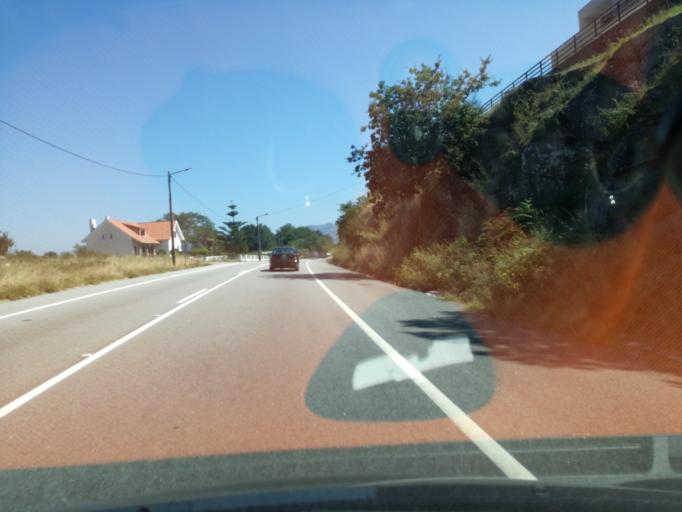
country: PT
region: Viana do Castelo
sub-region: Vila Nova de Cerveira
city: Vila Nova de Cerveira
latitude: 41.9133
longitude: -8.7854
